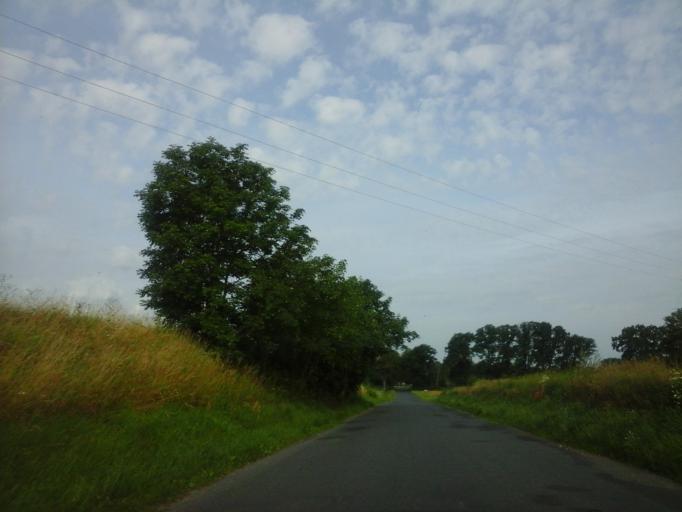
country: PL
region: West Pomeranian Voivodeship
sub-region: Powiat stargardzki
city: Dolice
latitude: 53.2666
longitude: 15.1545
